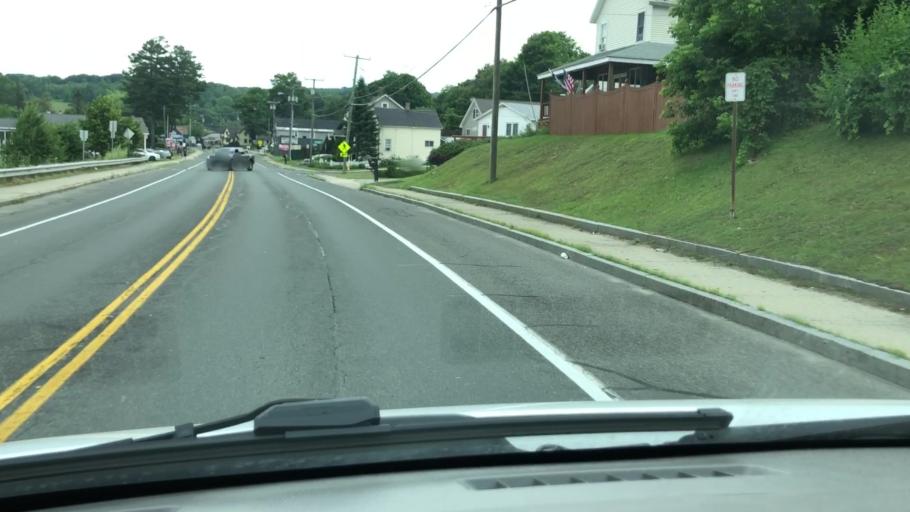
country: US
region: Massachusetts
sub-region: Berkshire County
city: Lanesborough
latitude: 42.4928
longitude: -73.2413
